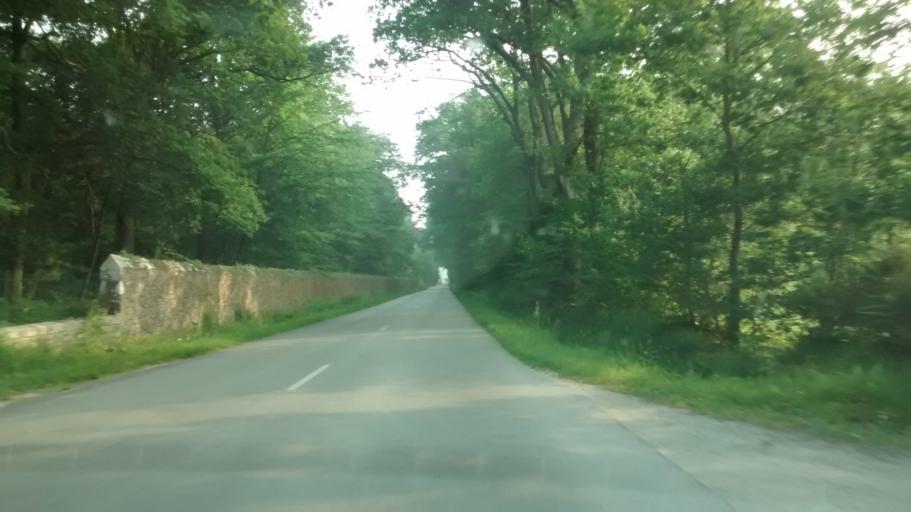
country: FR
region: Brittany
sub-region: Departement du Morbihan
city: Molac
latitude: 47.7567
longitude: -2.4376
